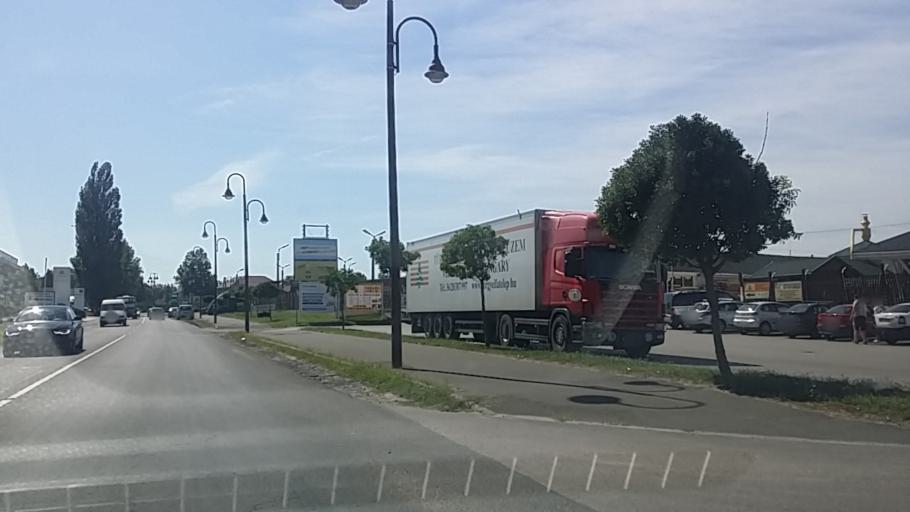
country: HU
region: Pest
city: Veresegyhaz
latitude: 47.6477
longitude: 19.2939
